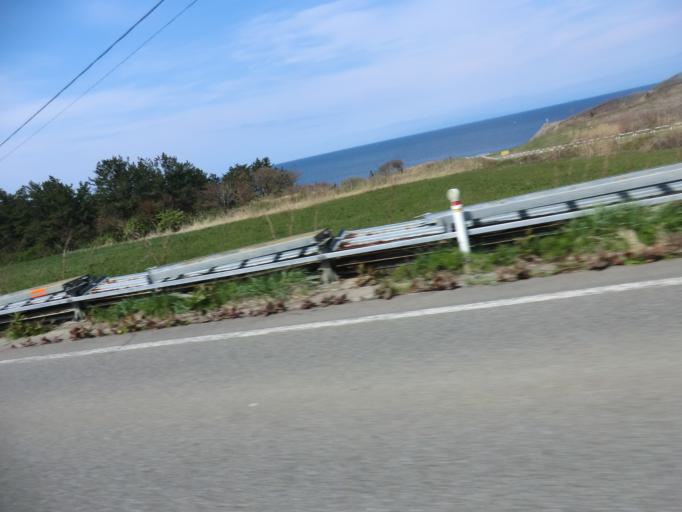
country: JP
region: Hokkaido
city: Hakodate
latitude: 41.4668
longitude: 140.8872
